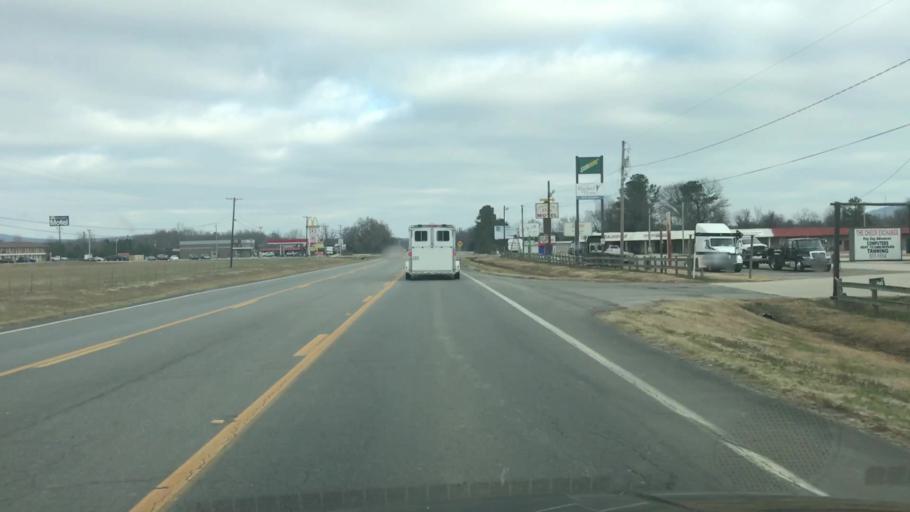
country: US
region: Arkansas
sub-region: Scott County
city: Waldron
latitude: 34.9017
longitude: -94.1074
